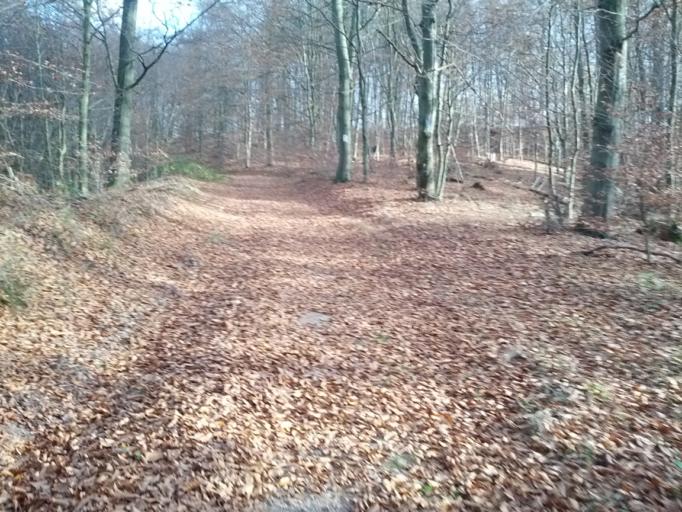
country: DE
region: Thuringia
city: Wolfsburg-Unkeroda
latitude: 50.9472
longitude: 10.2853
